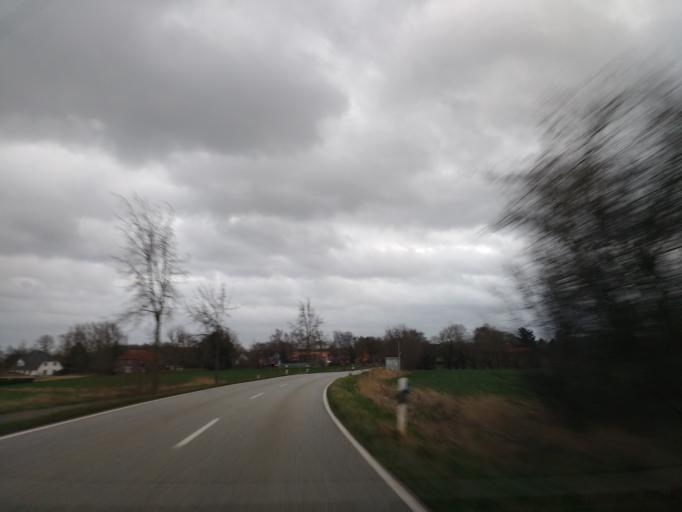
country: DE
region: Schleswig-Holstein
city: Neukirchen
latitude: 54.3627
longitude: 11.0331
